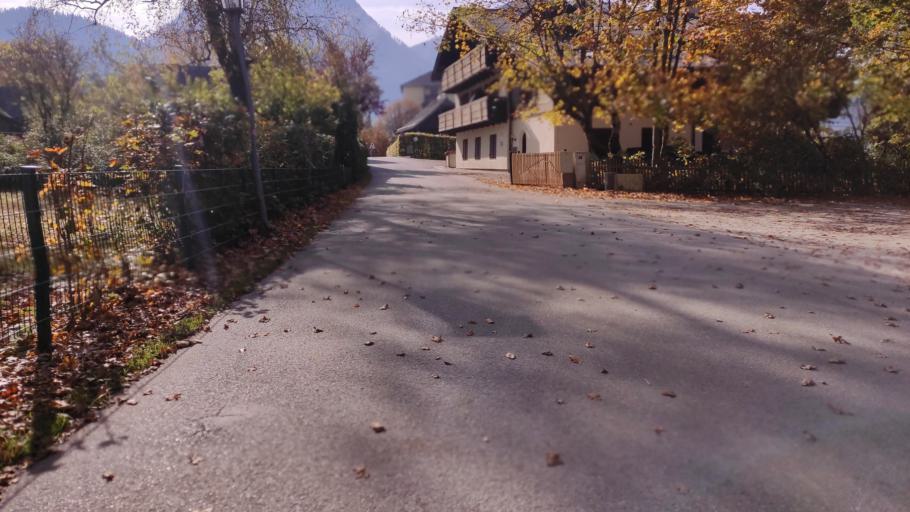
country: AT
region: Salzburg
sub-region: Politischer Bezirk Salzburg-Umgebung
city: Strobl
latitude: 47.7216
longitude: 13.4860
